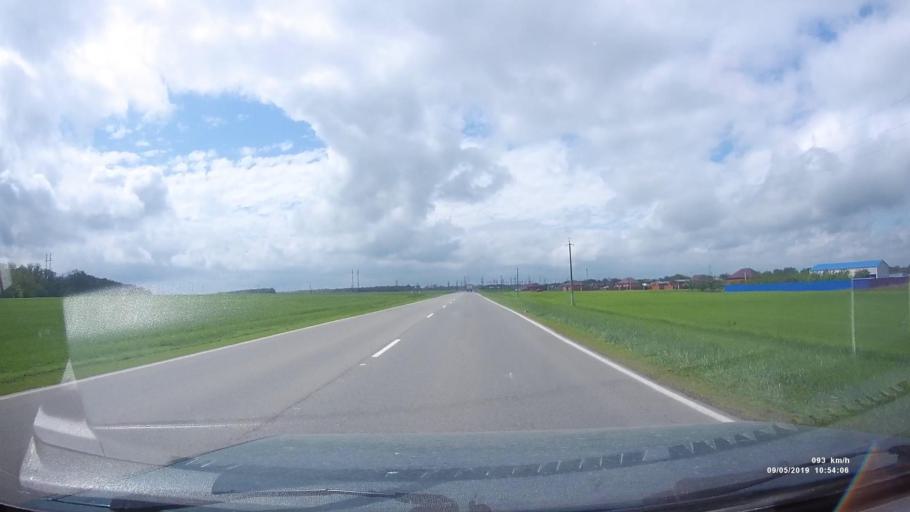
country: RU
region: Rostov
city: Peshkovo
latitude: 46.8814
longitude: 39.3345
